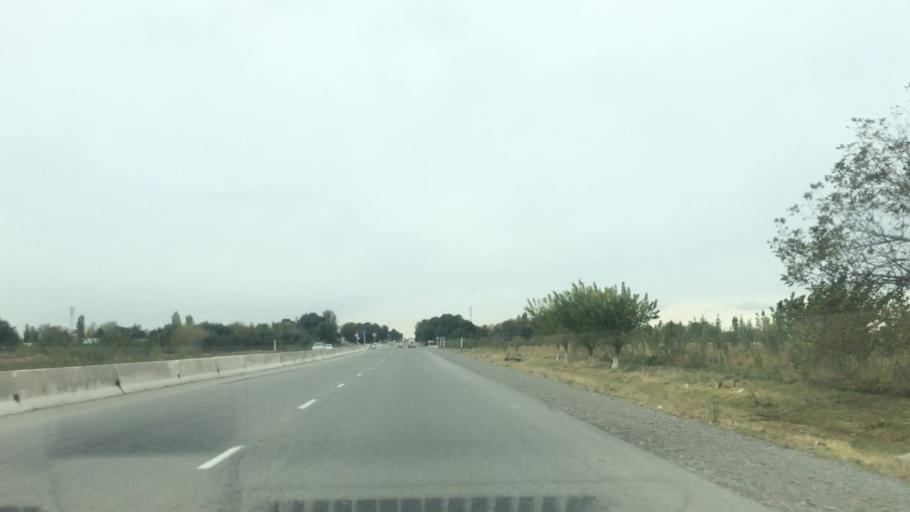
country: UZ
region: Samarqand
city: Bulung'ur
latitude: 39.7404
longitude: 67.1899
